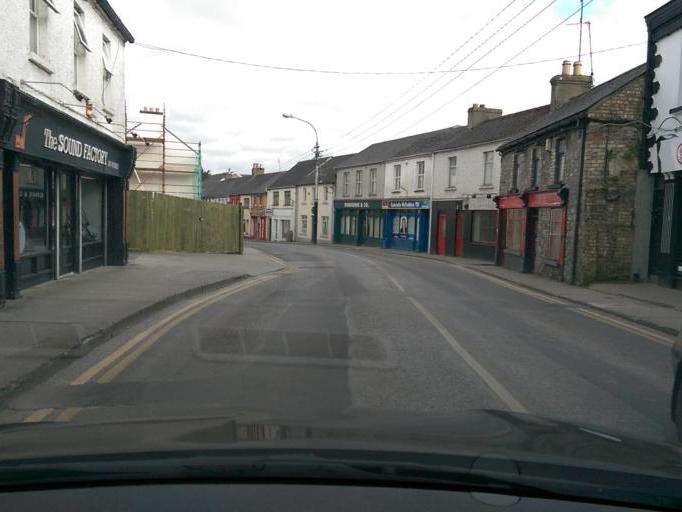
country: IE
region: Leinster
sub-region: An Iarmhi
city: Athlone
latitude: 53.4223
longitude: -7.9338
